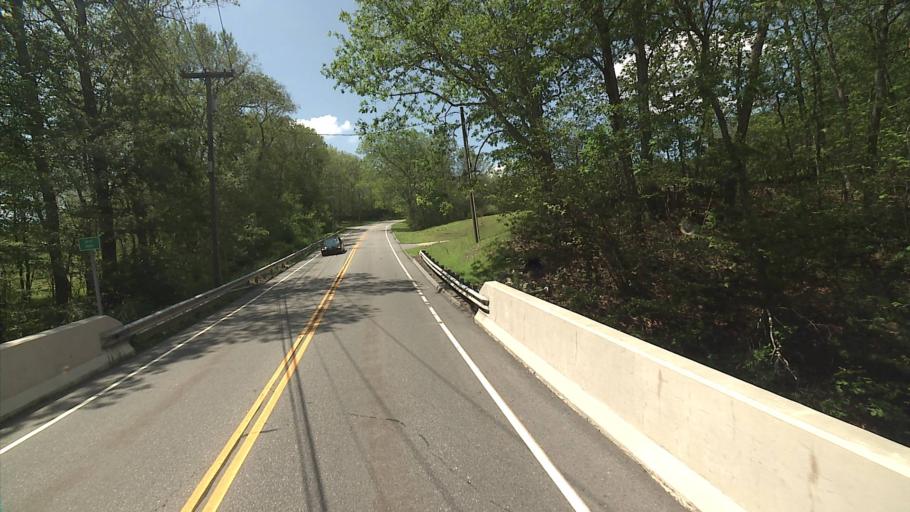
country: US
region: Connecticut
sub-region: New London County
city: Baltic
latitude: 41.7025
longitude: -72.0548
